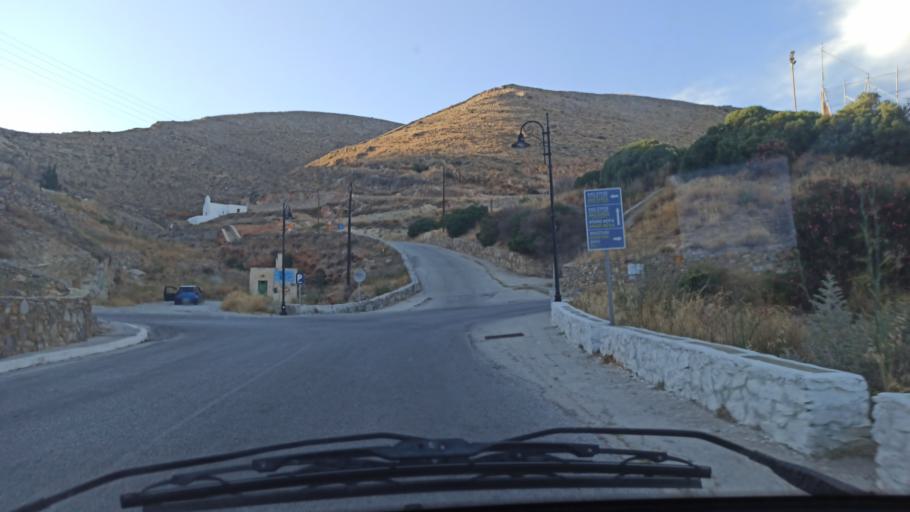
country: GR
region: South Aegean
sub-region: Nomos Kykladon
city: Ano Syros
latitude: 37.4526
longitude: 24.9367
